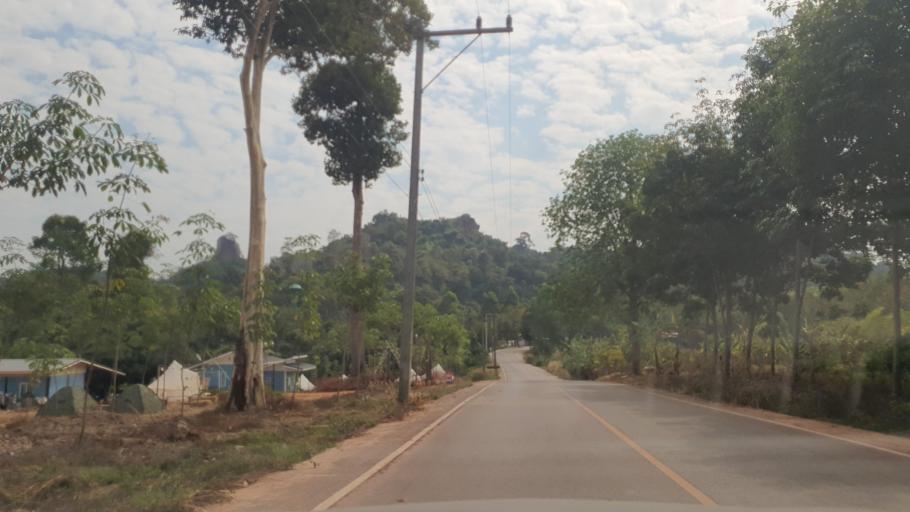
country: TH
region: Changwat Bueng Kan
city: Si Wilai
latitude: 18.2771
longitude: 103.7954
